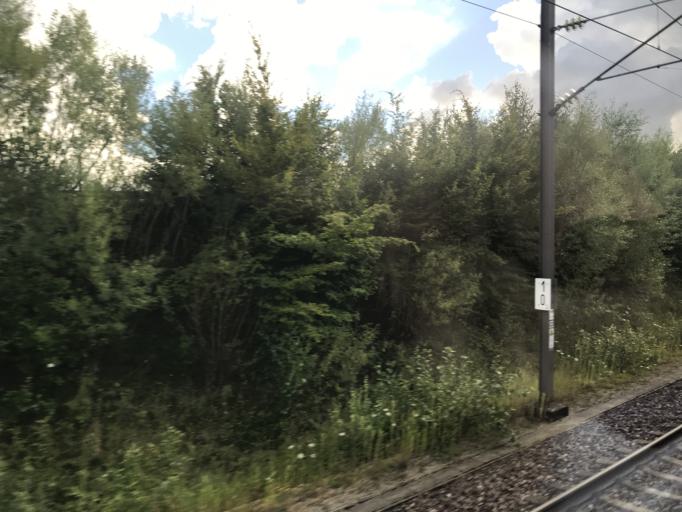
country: LU
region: Luxembourg
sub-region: Canton d'Esch-sur-Alzette
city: Petange
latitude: 49.5561
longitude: 5.8922
